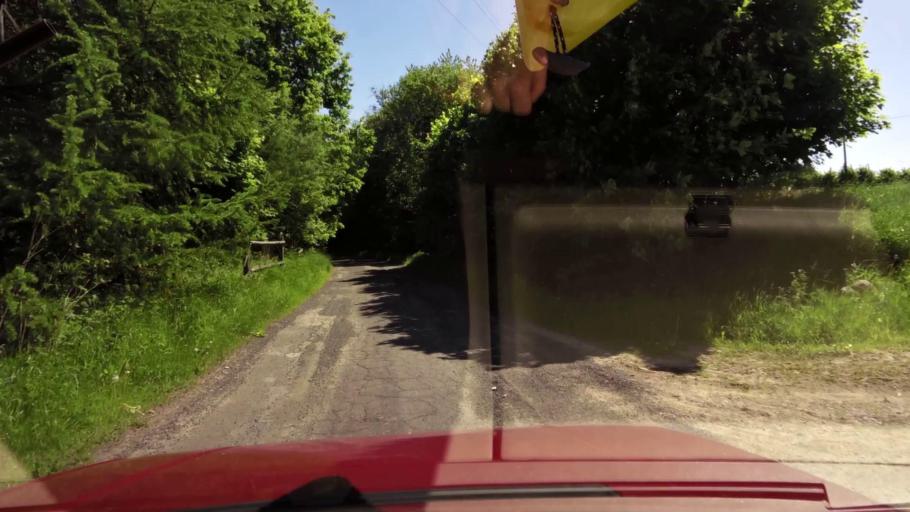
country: PL
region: West Pomeranian Voivodeship
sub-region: Powiat koszalinski
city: Polanow
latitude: 54.0386
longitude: 16.7659
